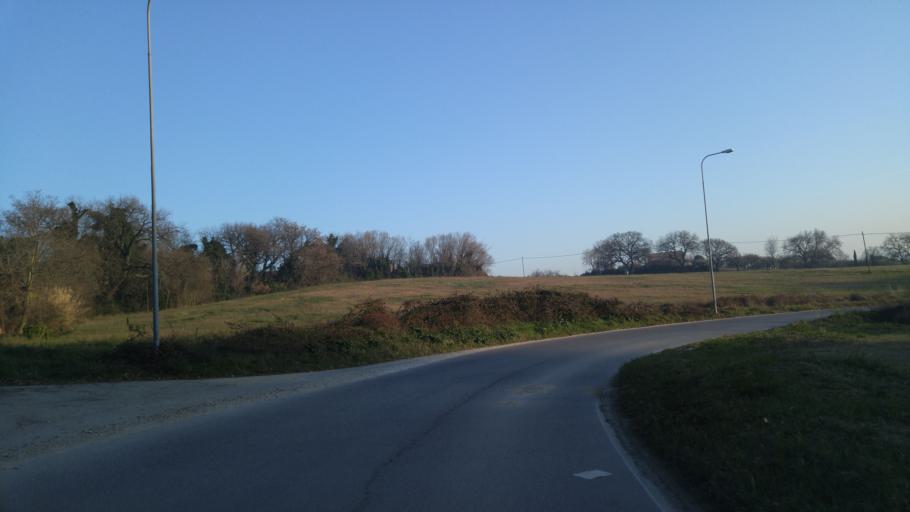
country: IT
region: The Marches
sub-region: Provincia di Pesaro e Urbino
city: Fenile
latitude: 43.8621
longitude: 12.9641
